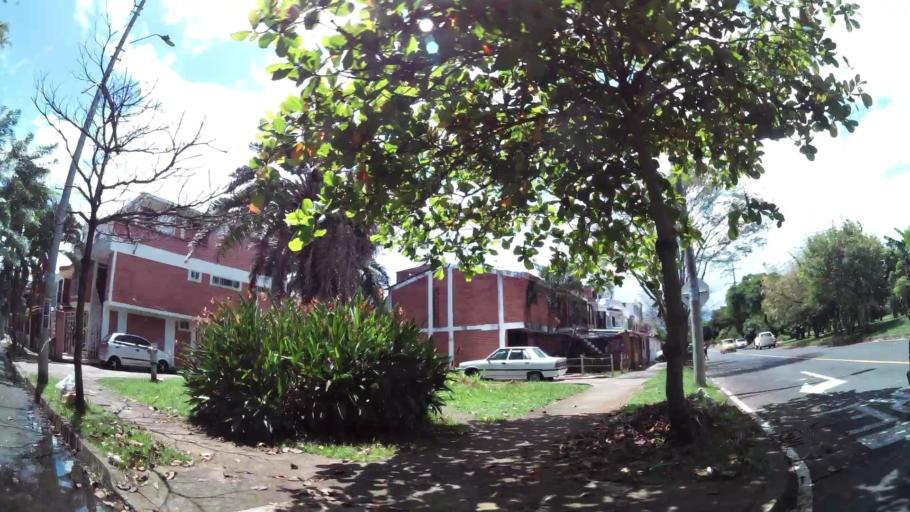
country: CO
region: Valle del Cauca
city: Cali
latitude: 3.3880
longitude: -76.5134
